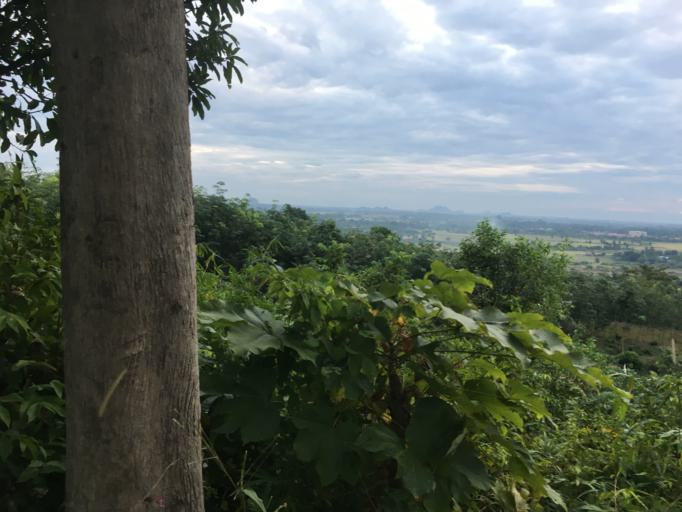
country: MM
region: Mon
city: Mawlamyine
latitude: 16.4744
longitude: 97.6302
